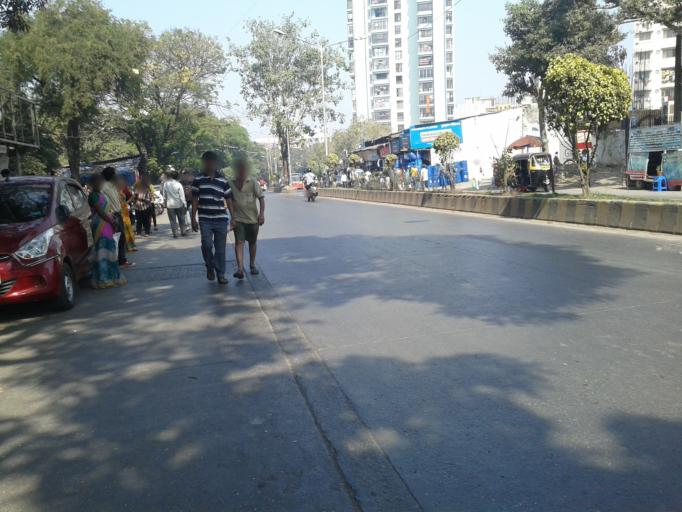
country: IN
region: Maharashtra
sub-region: Mumbai Suburban
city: Borivli
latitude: 19.2509
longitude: 72.8635
